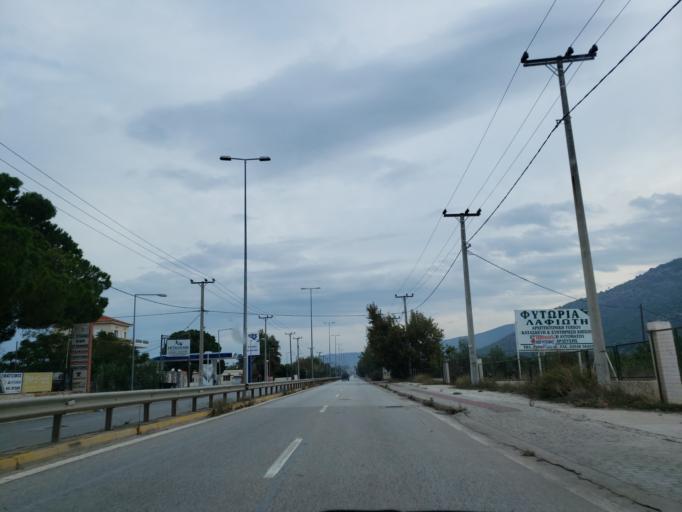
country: GR
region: Attica
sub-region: Nomarchia Anatolikis Attikis
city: Aghios Panteleimon
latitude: 38.1141
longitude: 23.9697
